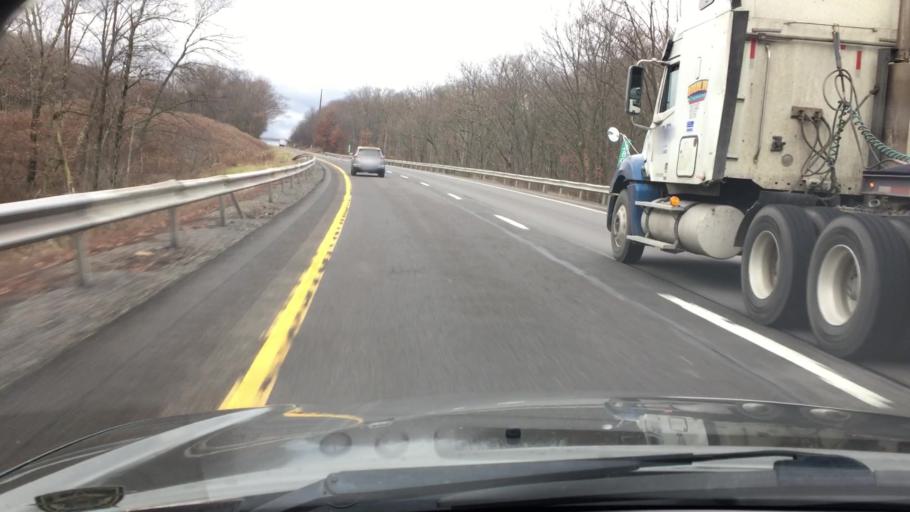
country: US
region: Pennsylvania
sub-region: Carbon County
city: Towamensing Trails
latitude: 41.0837
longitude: -75.6262
